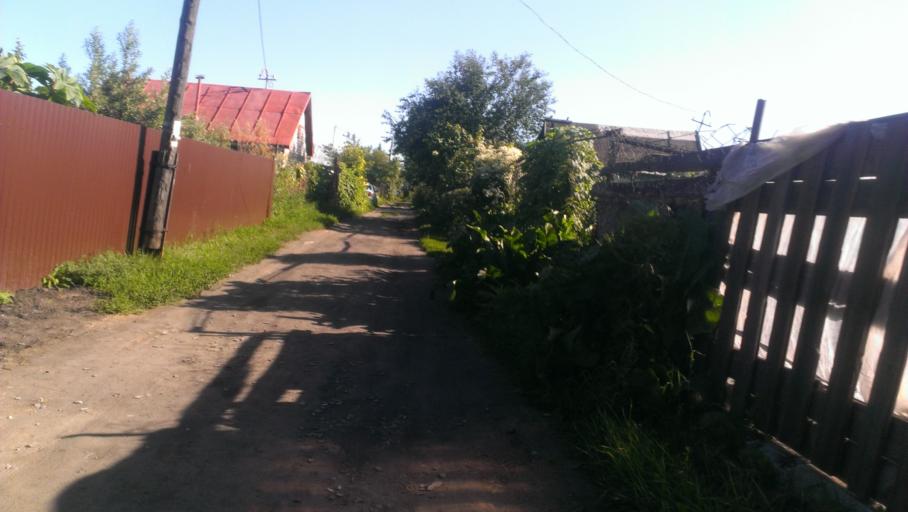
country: RU
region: Altai Krai
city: Novosilikatnyy
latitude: 53.3230
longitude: 83.6694
